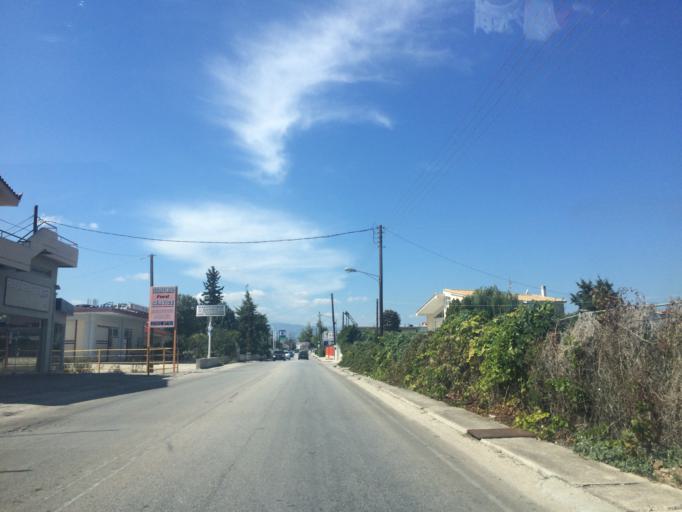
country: GR
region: Peloponnese
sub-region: Nomos Korinthias
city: Lekhaio
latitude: 37.9323
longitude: 22.8561
